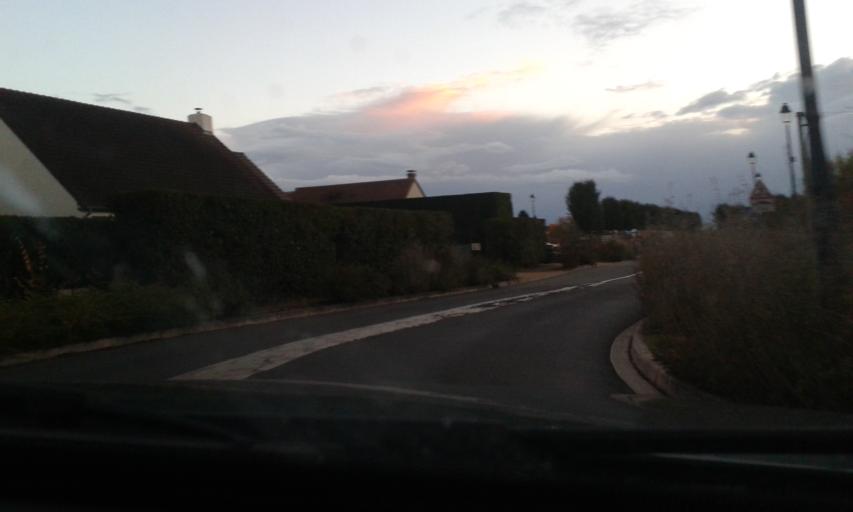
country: FR
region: Centre
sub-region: Departement du Loiret
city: Huisseau-sur-Mauves
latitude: 47.8913
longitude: 1.7064
